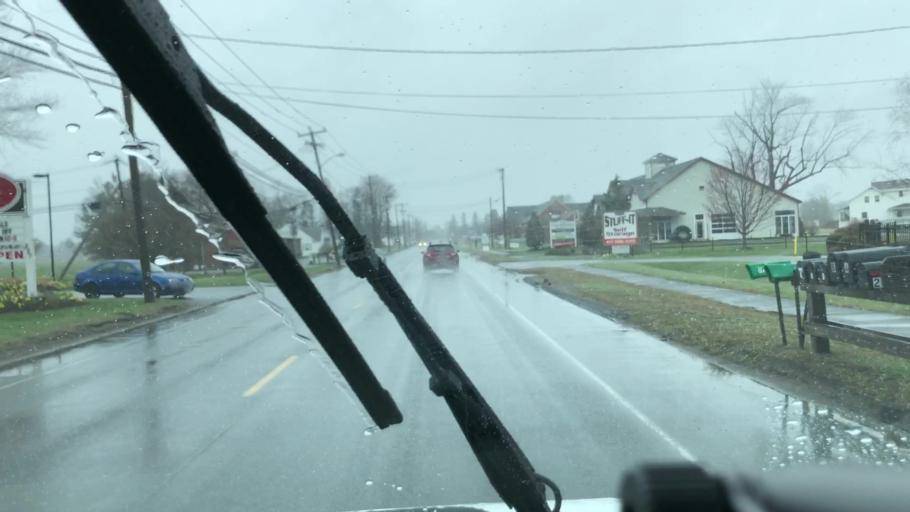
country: US
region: Massachusetts
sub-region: Hampshire County
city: Hadley
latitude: 42.3462
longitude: -72.5744
